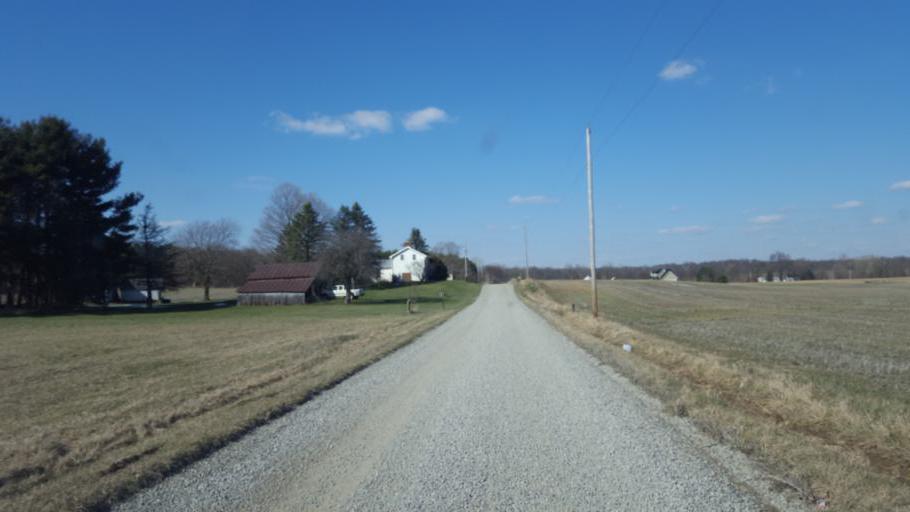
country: US
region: Ohio
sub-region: Morrow County
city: Mount Gilead
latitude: 40.4686
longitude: -82.7447
